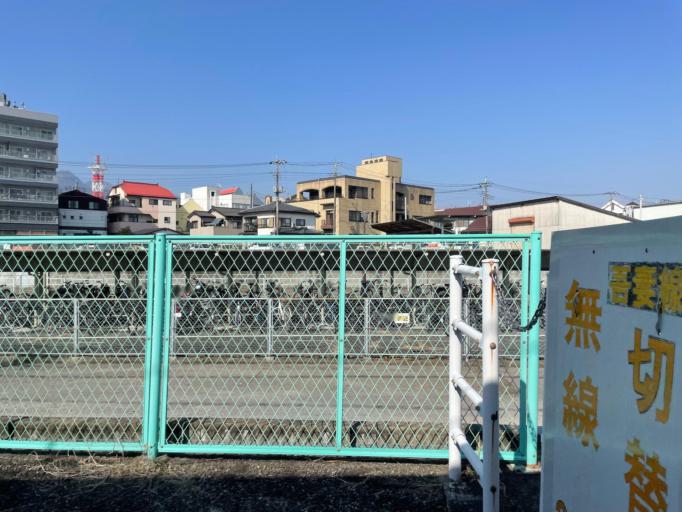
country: JP
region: Gunma
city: Shibukawa
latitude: 36.4920
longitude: 139.0089
